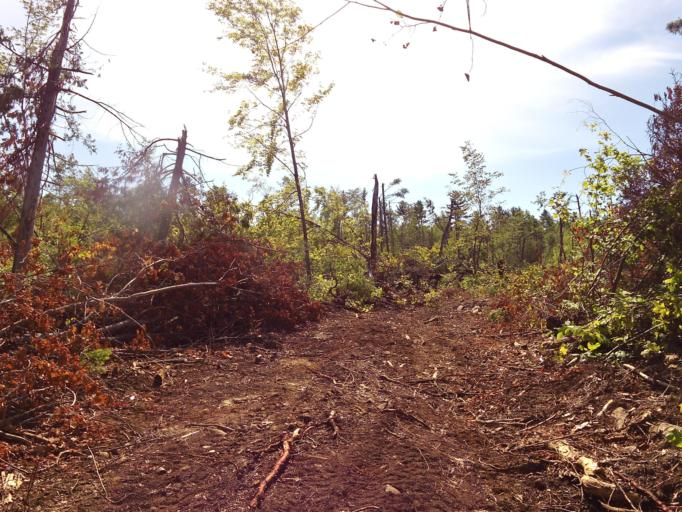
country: CA
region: Ontario
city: Renfrew
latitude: 45.1265
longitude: -76.7260
